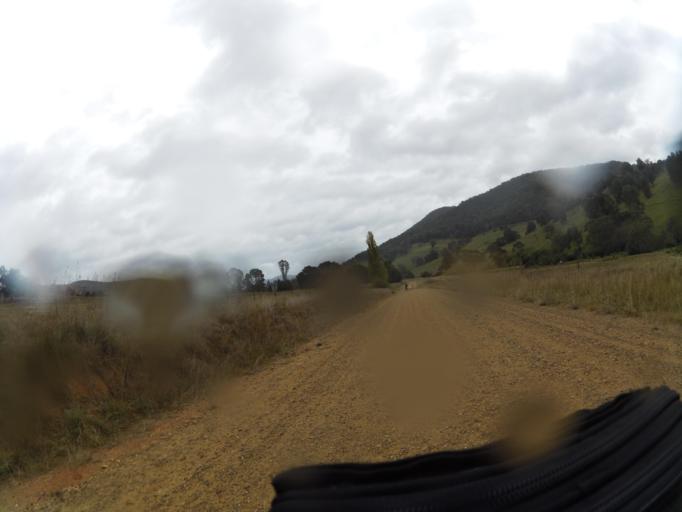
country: AU
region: New South Wales
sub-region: Greater Hume Shire
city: Holbrook
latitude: -36.2380
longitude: 147.6315
